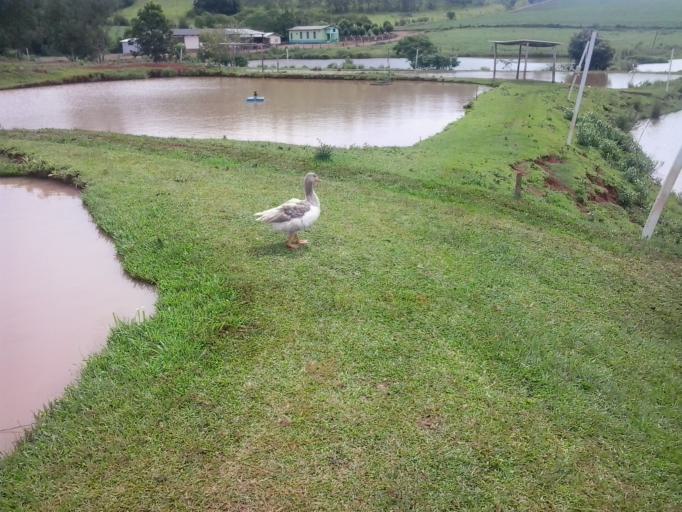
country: BR
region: Parana
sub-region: Dois Vizinhos
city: Dois Vizinhos
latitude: -25.8232
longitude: -53.2117
